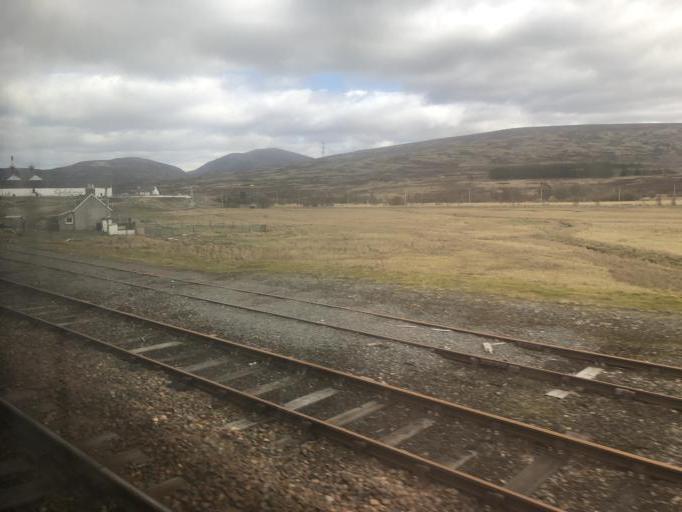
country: GB
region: Scotland
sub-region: Highland
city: Kingussie
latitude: 56.9378
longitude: -4.2441
